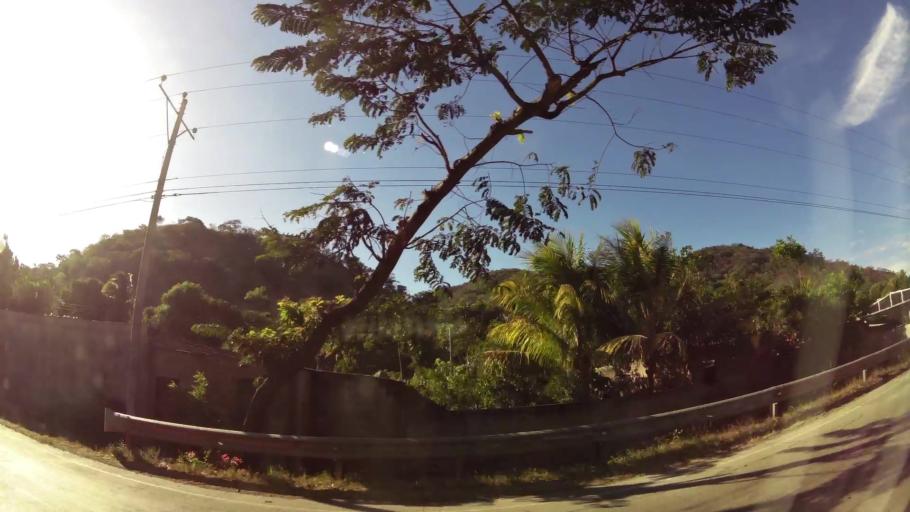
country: SV
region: Santa Ana
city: Santa Ana
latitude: 14.0460
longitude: -89.5184
